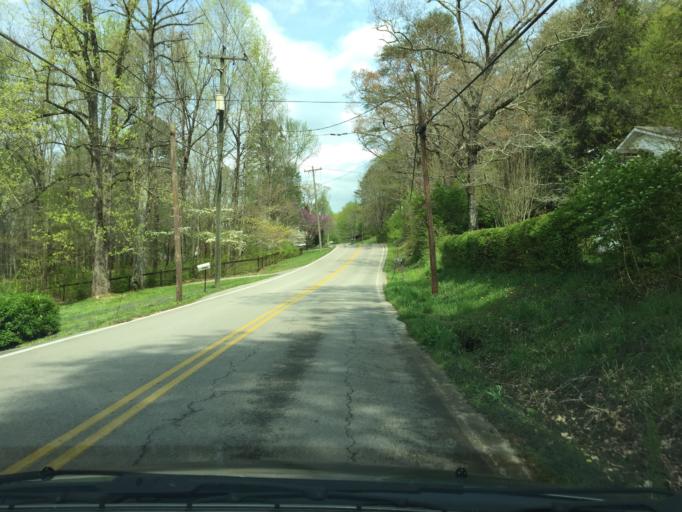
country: US
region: Tennessee
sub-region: Hamilton County
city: Walden
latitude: 35.1659
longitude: -85.2746
